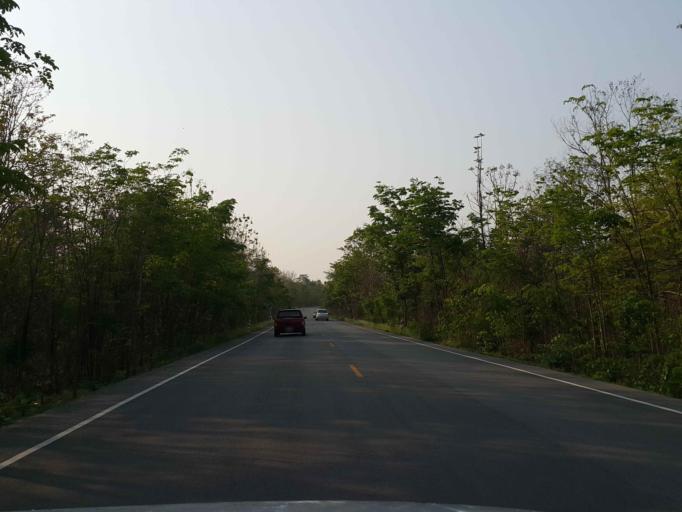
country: TH
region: Sukhothai
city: Thung Saliam
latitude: 17.3757
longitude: 99.4024
